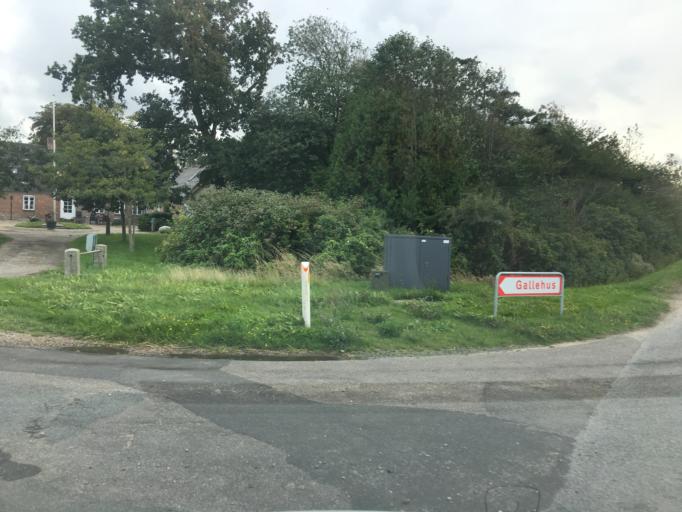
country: DE
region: Schleswig-Holstein
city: Aventoft
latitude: 54.9597
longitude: 8.8095
